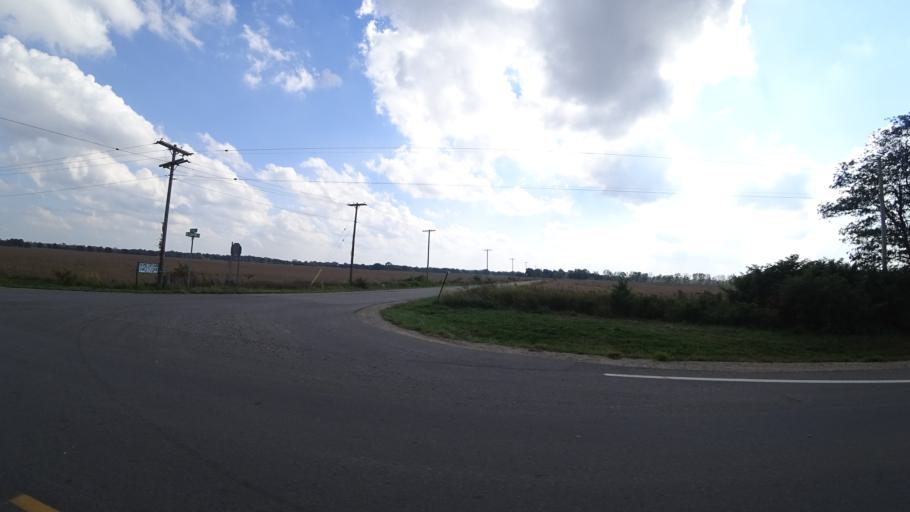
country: US
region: Michigan
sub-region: Calhoun County
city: Athens
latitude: 42.0641
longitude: -85.1959
